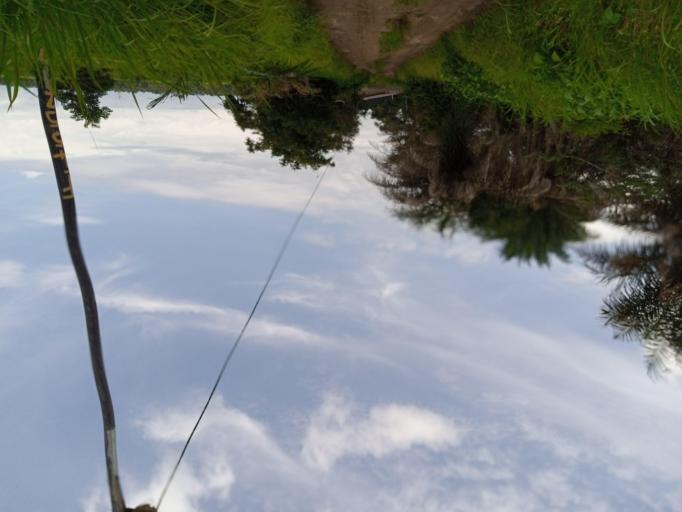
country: SL
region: Northern Province
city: Masoyila
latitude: 8.5920
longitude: -13.1697
